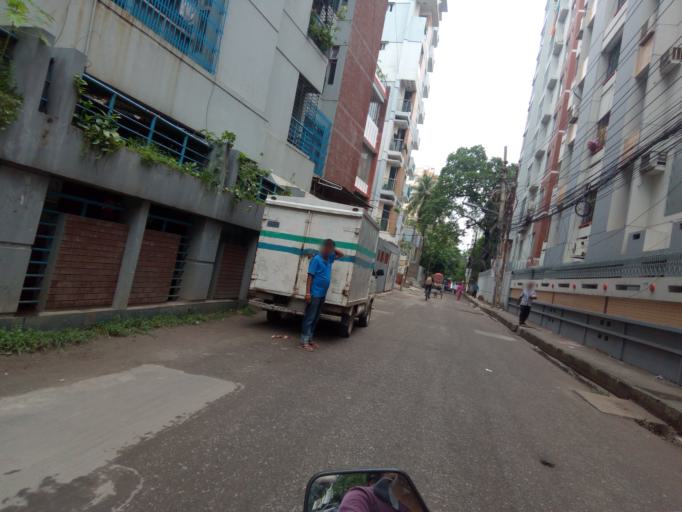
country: BD
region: Dhaka
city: Azimpur
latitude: 23.7547
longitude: 90.3713
